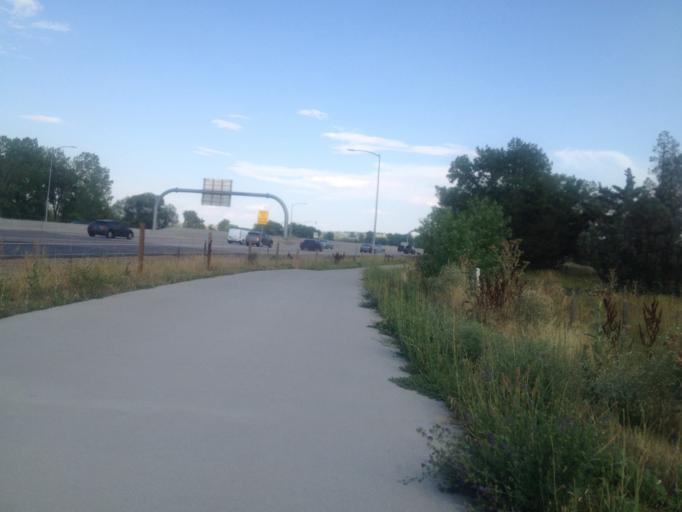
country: US
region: Colorado
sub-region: Boulder County
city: Boulder
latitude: 39.9834
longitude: -105.2287
